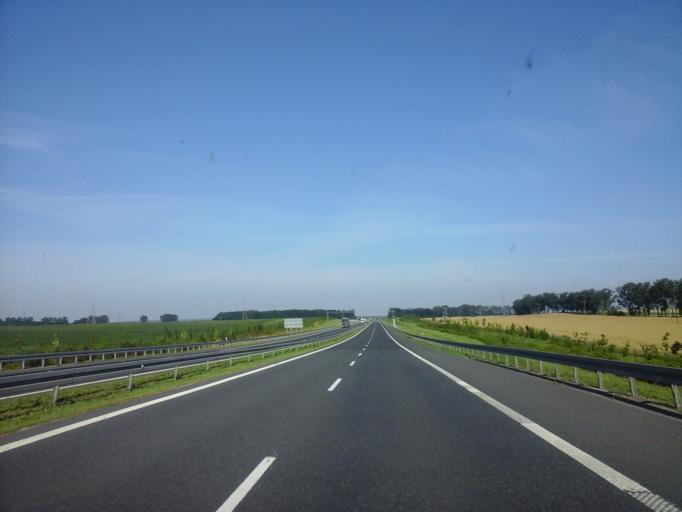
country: PL
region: West Pomeranian Voivodeship
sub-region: Powiat stargardzki
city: Stargard Szczecinski
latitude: 53.3084
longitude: 15.0169
